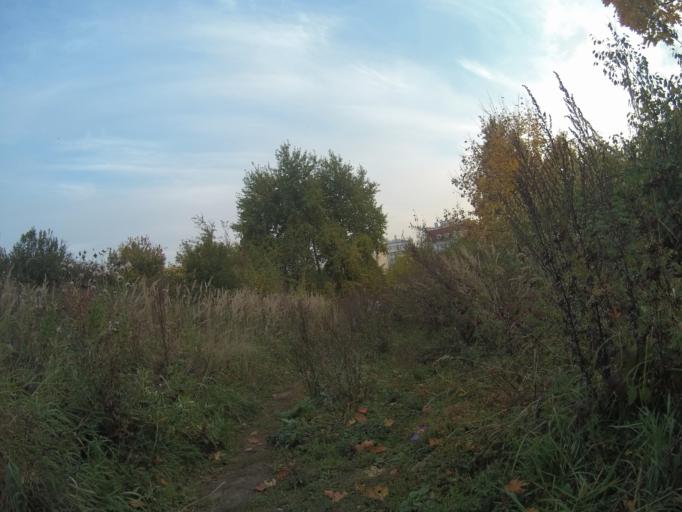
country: RU
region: Vladimir
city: Vladimir
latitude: 56.1341
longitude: 40.3909
